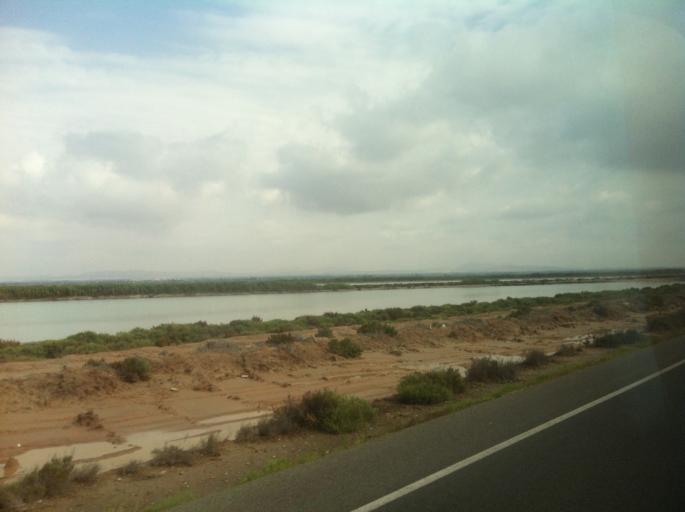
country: ES
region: Valencia
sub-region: Provincia de Alicante
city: Santa Pola
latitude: 38.1738
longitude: -0.6234
